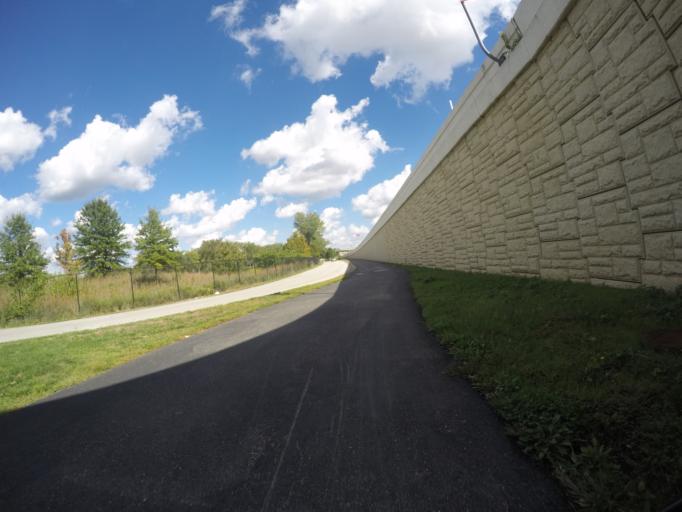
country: US
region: Kansas
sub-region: Johnson County
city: Overland Park
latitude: 38.9349
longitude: -94.6856
